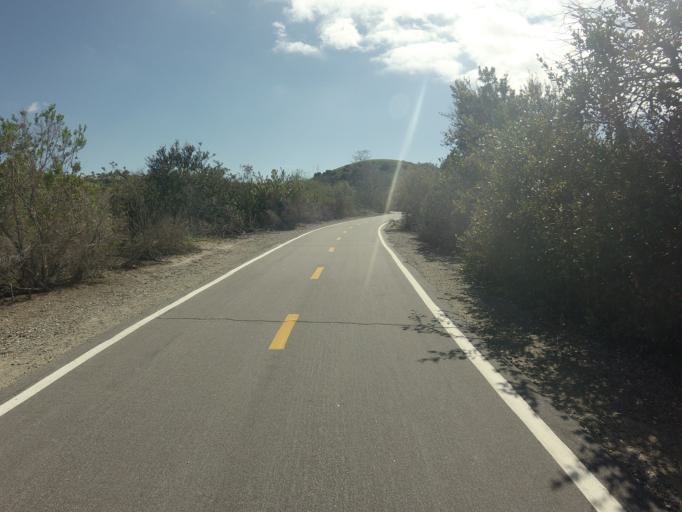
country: US
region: California
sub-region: Orange County
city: Aliso Viejo
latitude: 33.5533
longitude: -117.7192
